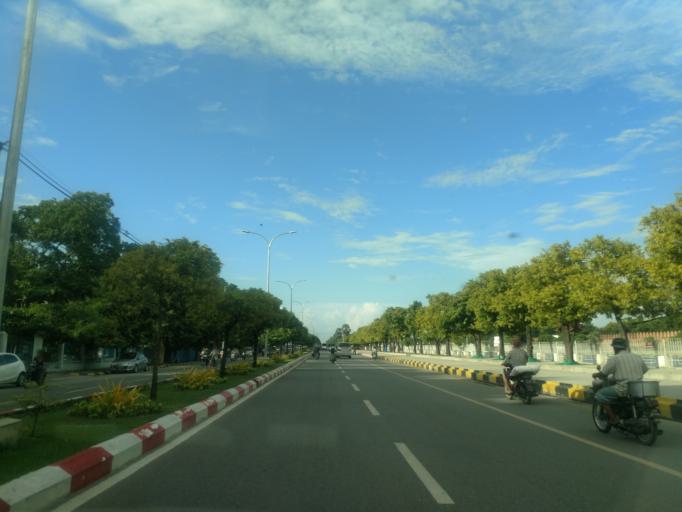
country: MM
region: Mandalay
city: Mandalay
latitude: 21.9865
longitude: 96.0846
